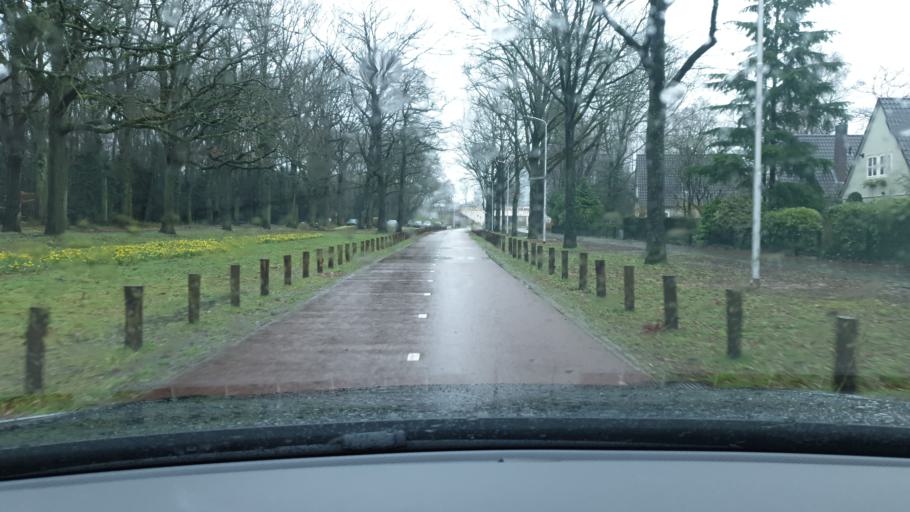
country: NL
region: North Brabant
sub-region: Gemeente Eindhoven
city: Eindhoven
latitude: 51.4547
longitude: 5.4466
